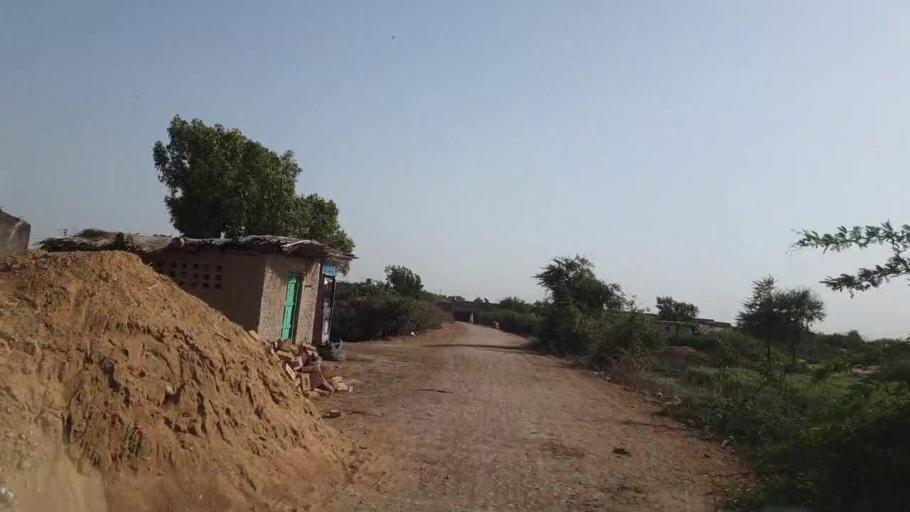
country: PK
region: Sindh
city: Tando Ghulam Ali
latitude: 25.0722
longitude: 68.8609
